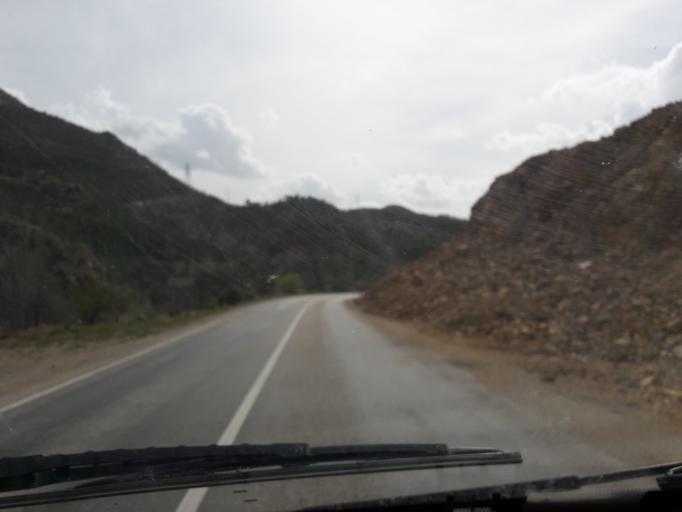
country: TR
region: Gumushane
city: Kale
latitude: 40.3952
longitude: 39.5963
